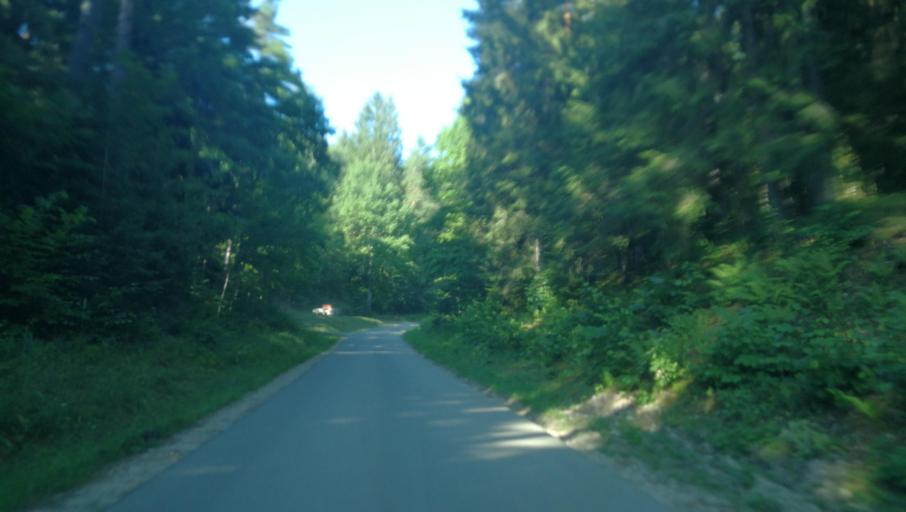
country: LV
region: Cesu Rajons
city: Cesis
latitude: 57.2850
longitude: 25.2142
